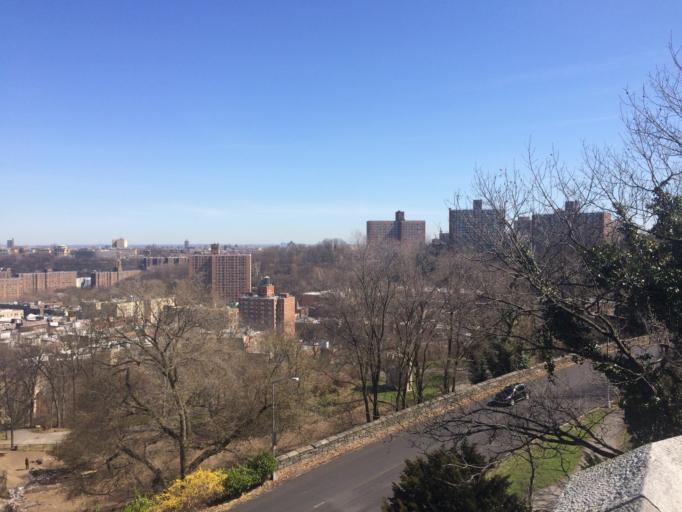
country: US
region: New York
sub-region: New York County
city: Inwood
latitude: 40.8619
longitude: -73.9328
